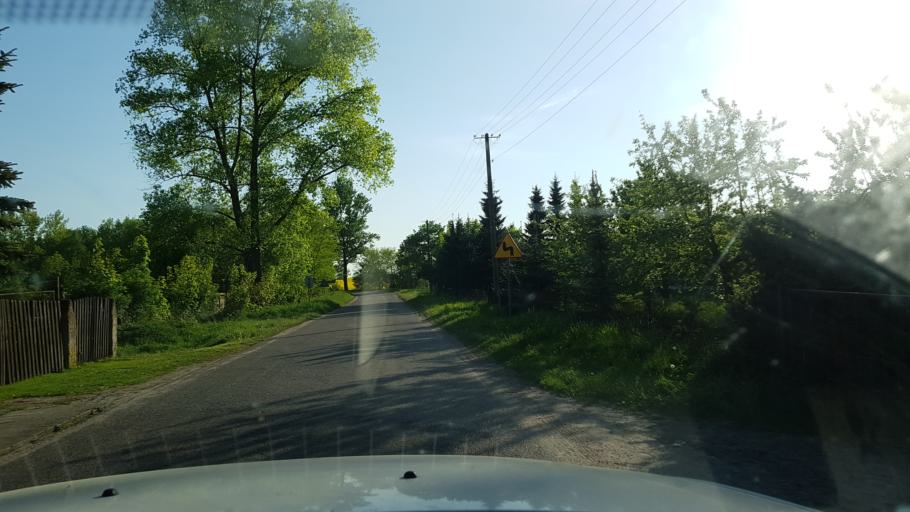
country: PL
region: West Pomeranian Voivodeship
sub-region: Powiat lobeski
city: Dobra
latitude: 53.6317
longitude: 15.3596
